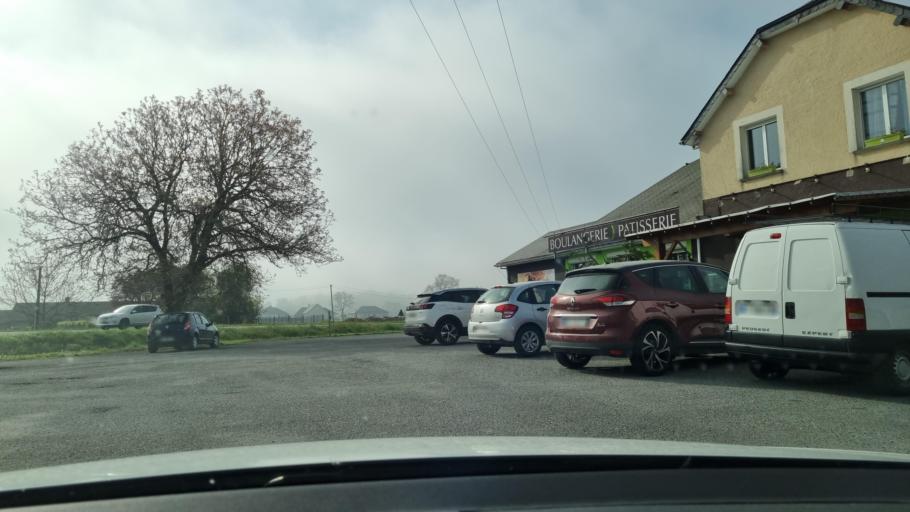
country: FR
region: Aquitaine
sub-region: Departement des Pyrenees-Atlantiques
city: Soumoulou
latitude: 43.2441
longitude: -0.1638
